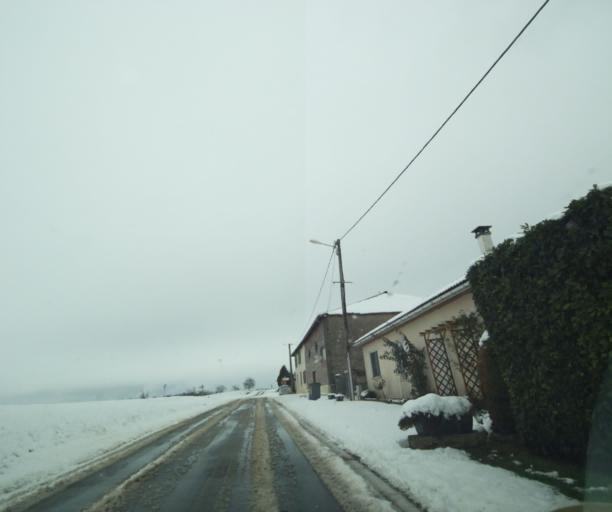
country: FR
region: Champagne-Ardenne
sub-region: Departement de la Haute-Marne
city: Montier-en-Der
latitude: 48.4138
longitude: 4.7405
